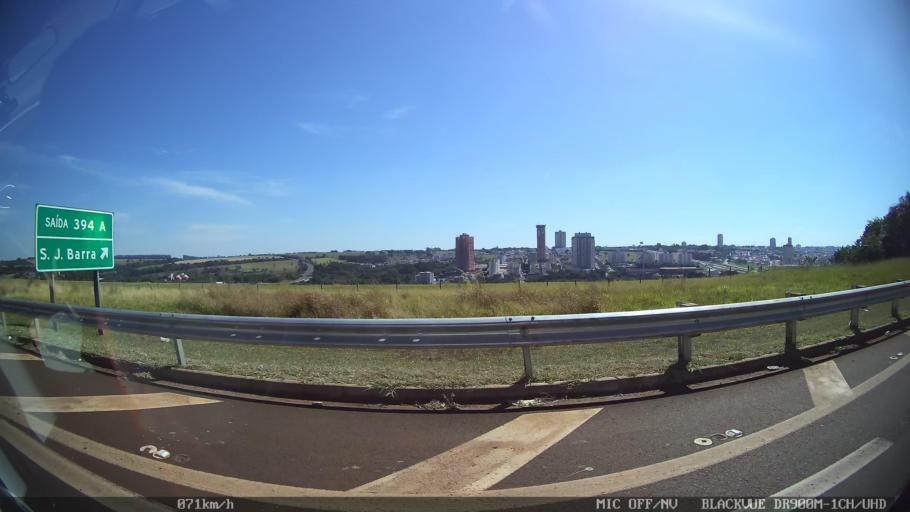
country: BR
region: Sao Paulo
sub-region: Franca
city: Franca
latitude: -20.5595
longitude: -47.4098
